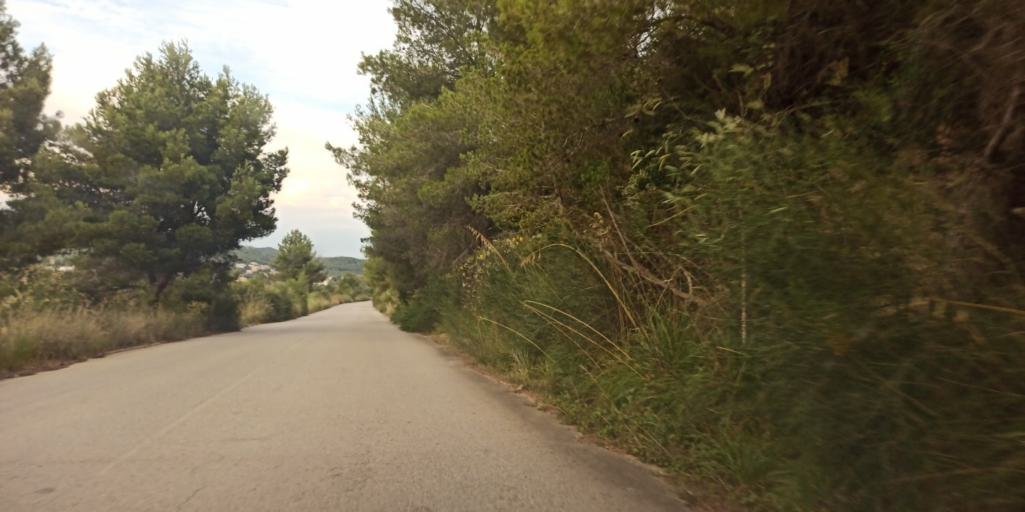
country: ES
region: Catalonia
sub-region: Provincia de Barcelona
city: Castelldefels
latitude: 41.2927
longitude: 1.9630
